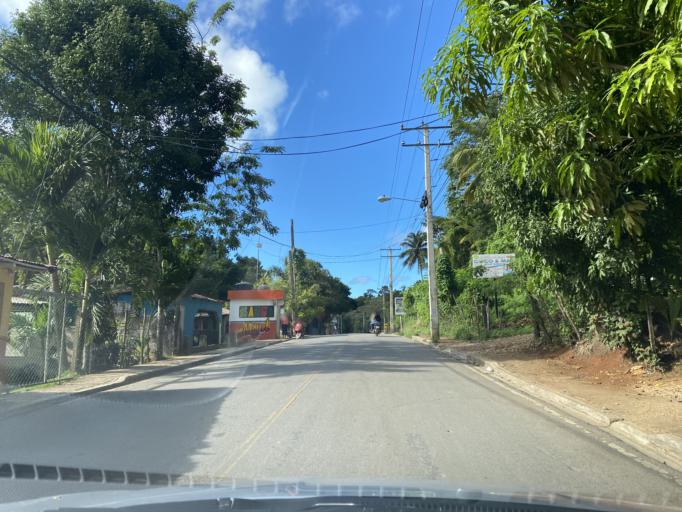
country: DO
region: Samana
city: Las Terrenas
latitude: 19.2956
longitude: -69.5499
